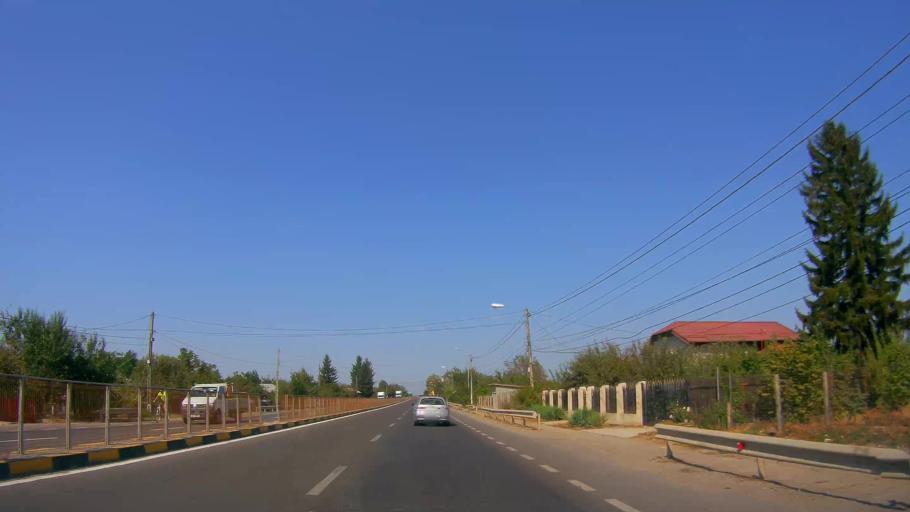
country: RO
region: Giurgiu
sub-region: Comuna Fratesti
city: Remus
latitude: 43.9391
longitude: 25.9779
